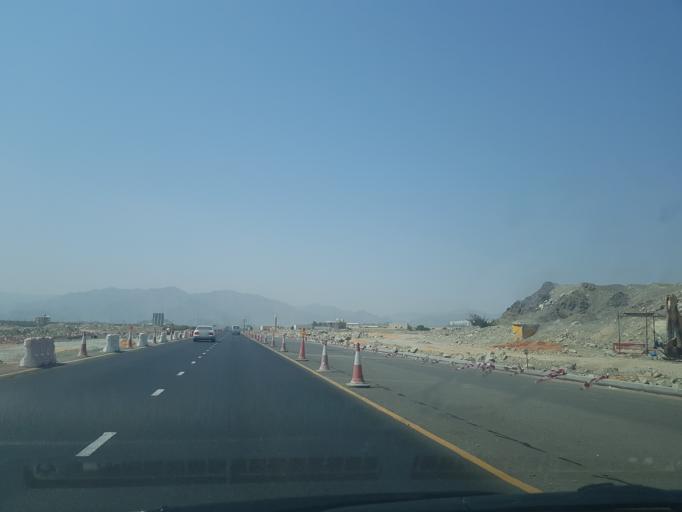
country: AE
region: Al Fujayrah
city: Al Fujayrah
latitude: 25.1223
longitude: 56.3117
